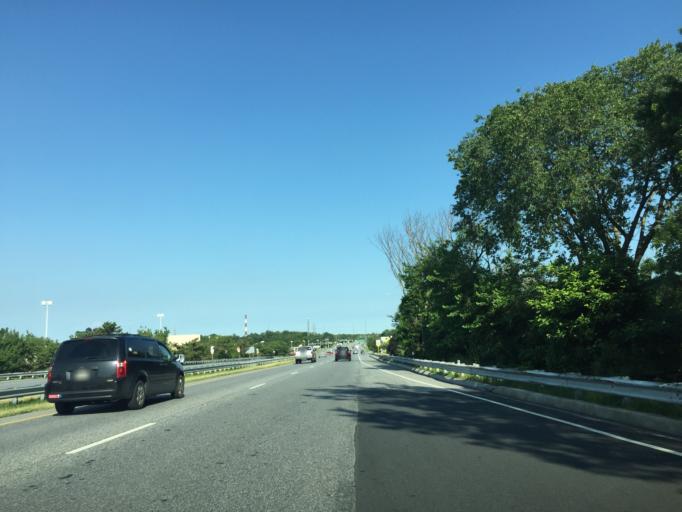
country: US
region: Maryland
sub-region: Baltimore County
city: Rosedale
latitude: 39.2926
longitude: -76.5148
